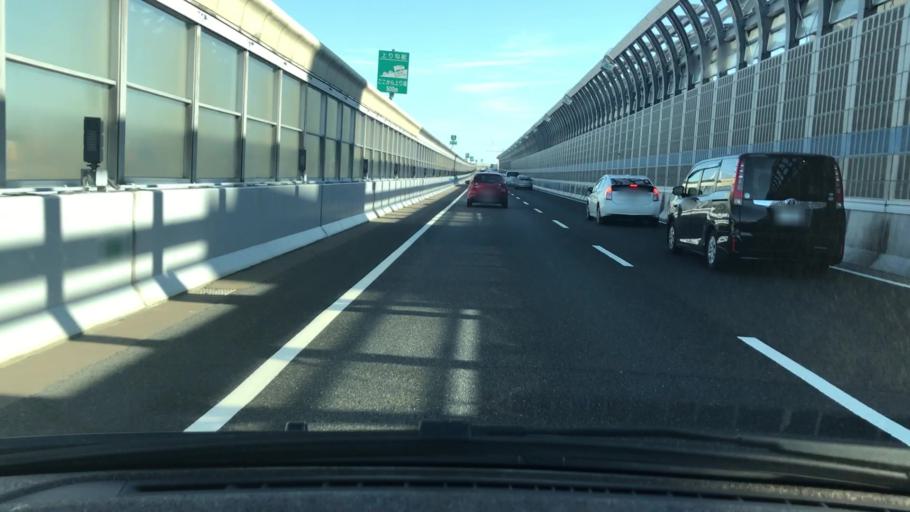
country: JP
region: Hyogo
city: Ashiya
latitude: 34.7231
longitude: 135.2969
